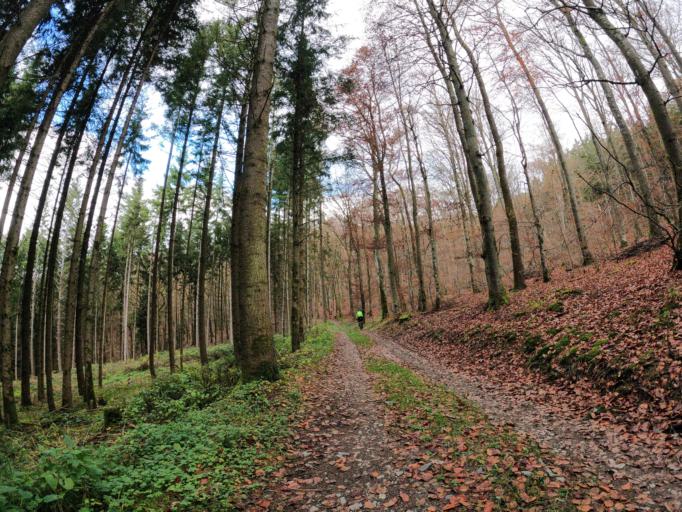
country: LU
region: Diekirch
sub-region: Canton de Wiltz
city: Winseler
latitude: 49.9914
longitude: 5.8672
